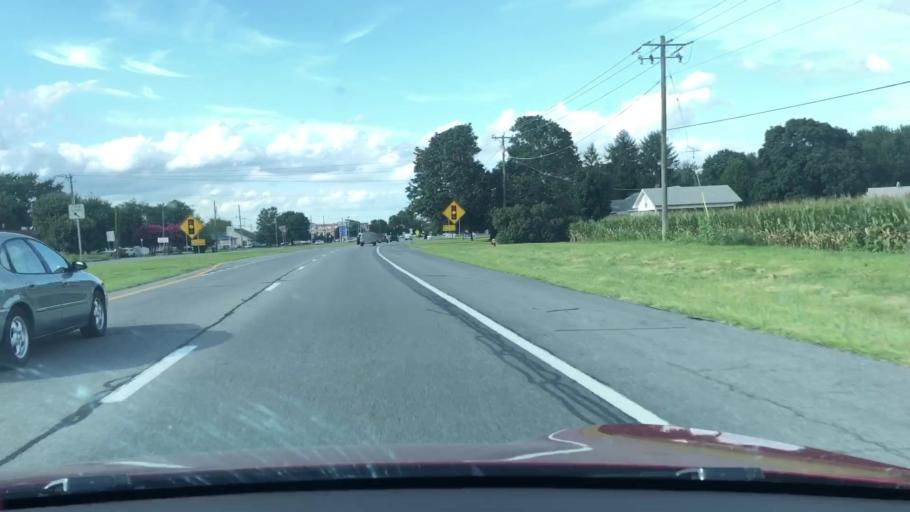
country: US
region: Delaware
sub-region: Kent County
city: Felton
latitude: 39.0028
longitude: -75.5692
